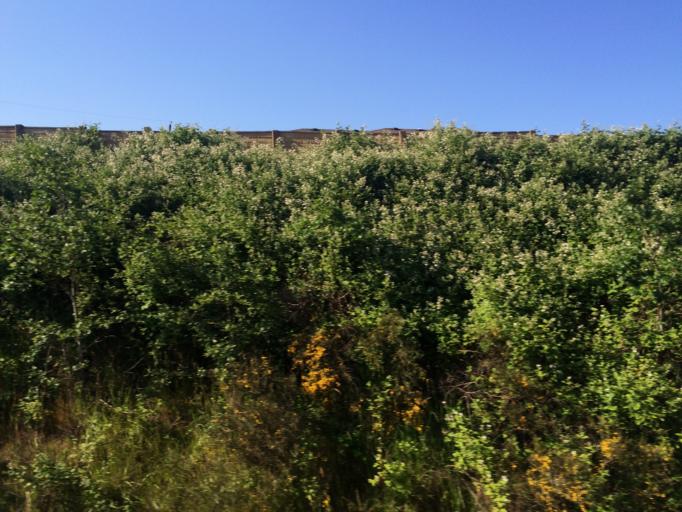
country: CA
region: British Columbia
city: Victoria
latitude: 48.4641
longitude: -123.4260
